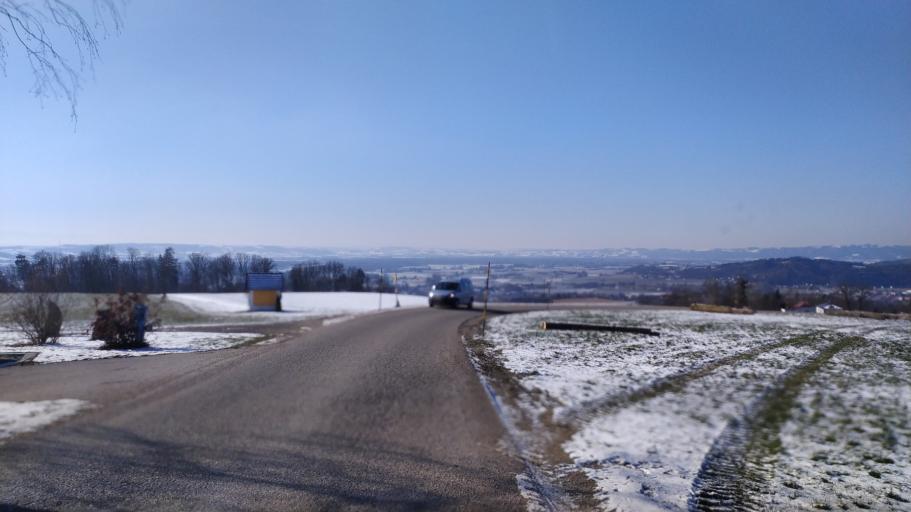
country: AT
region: Upper Austria
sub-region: Politischer Bezirk Urfahr-Umgebung
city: Ottensheim
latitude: 48.3452
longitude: 14.1999
